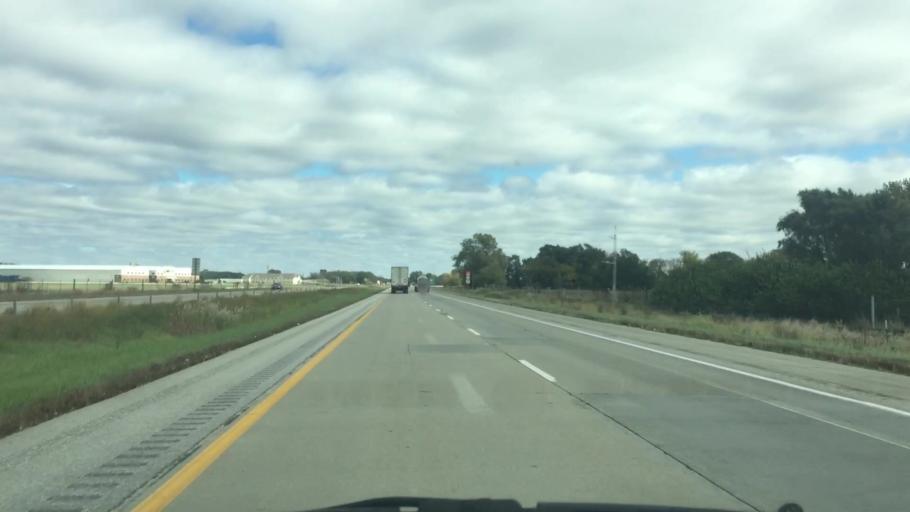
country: US
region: Iowa
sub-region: Jasper County
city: Colfax
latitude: 41.6884
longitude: -93.2615
